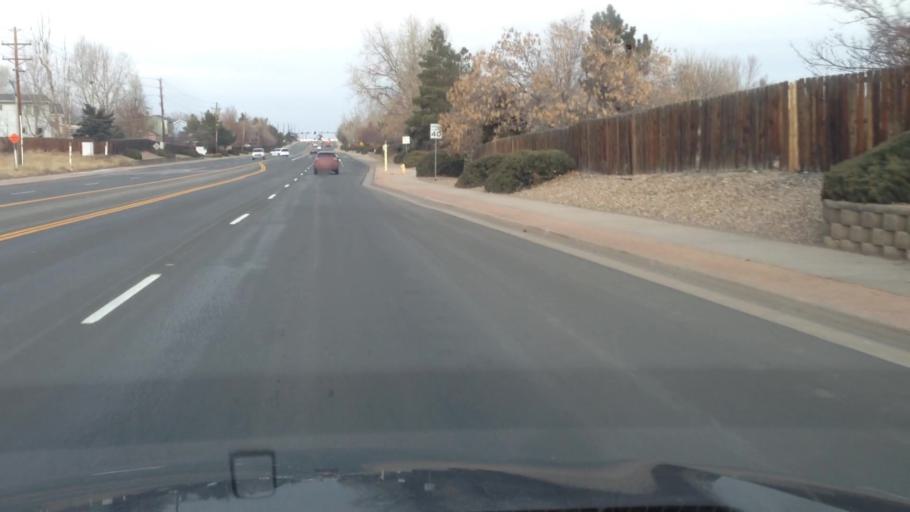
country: US
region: Colorado
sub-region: Douglas County
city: Stonegate
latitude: 39.5605
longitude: -104.7969
